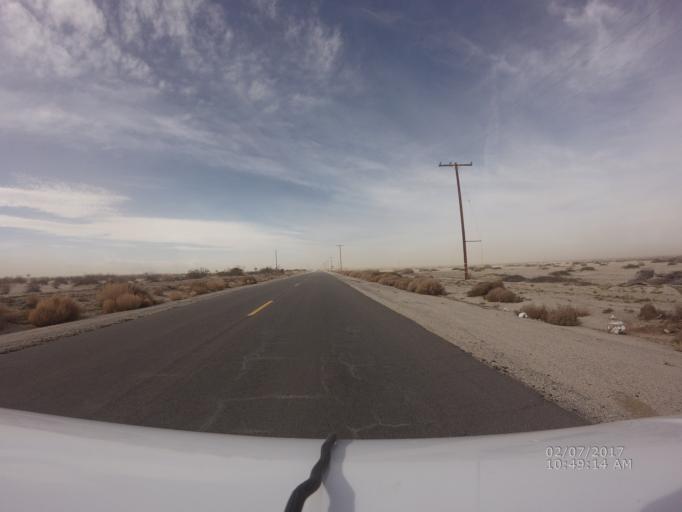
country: US
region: California
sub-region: Los Angeles County
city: Lake Los Angeles
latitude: 34.6901
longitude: -117.8763
